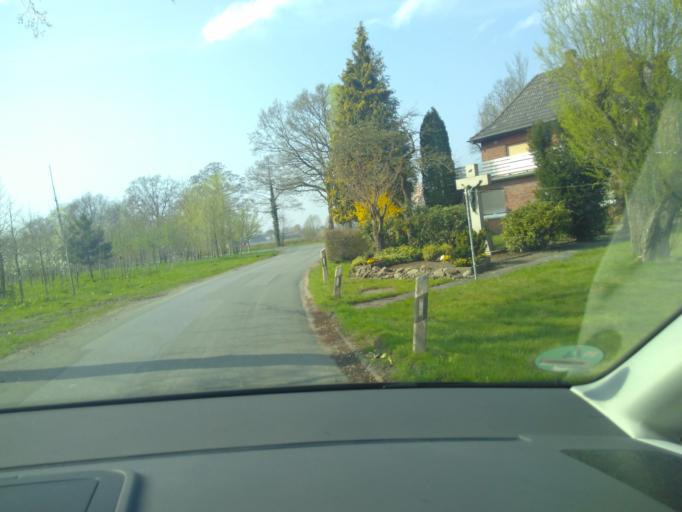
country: DE
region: North Rhine-Westphalia
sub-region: Regierungsbezirk Detmold
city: Verl
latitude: 51.8632
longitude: 8.4850
